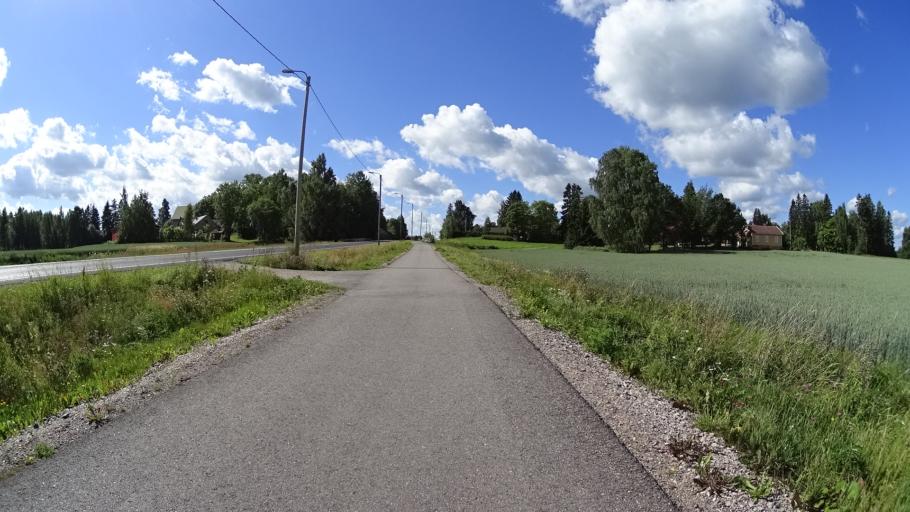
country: FI
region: Uusimaa
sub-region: Helsinki
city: Jaervenpaeae
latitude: 60.4404
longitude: 25.0720
